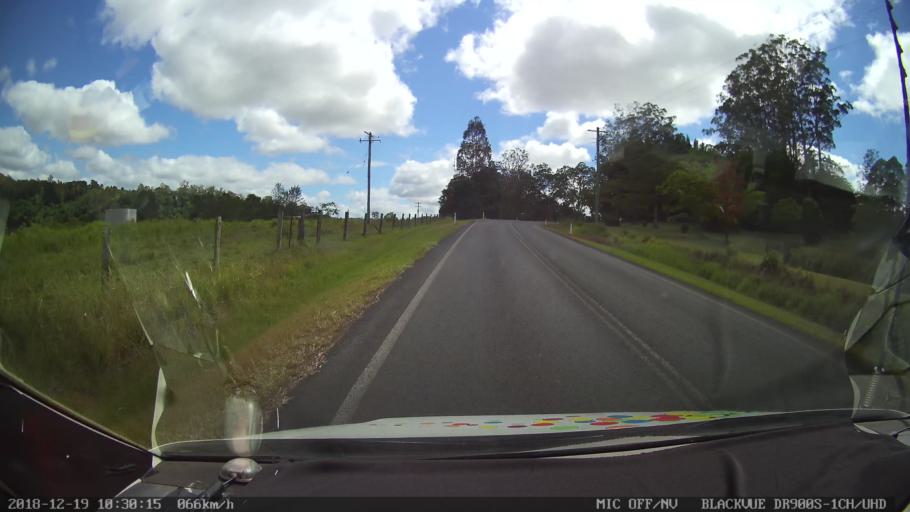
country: AU
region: New South Wales
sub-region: Lismore Municipality
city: Larnook
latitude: -28.5898
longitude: 153.1057
